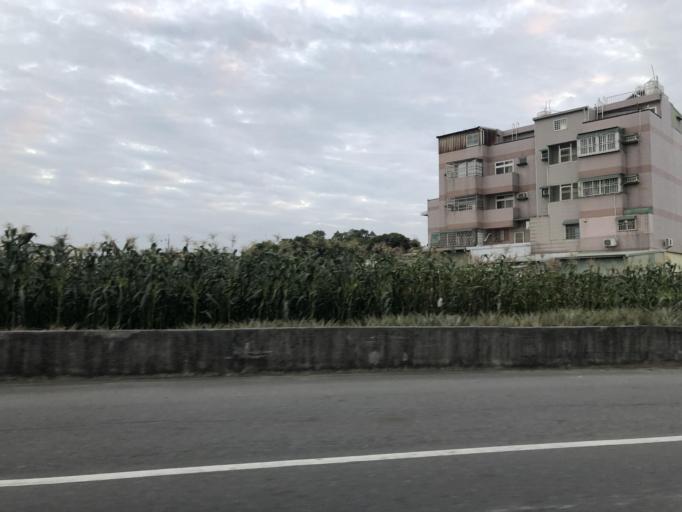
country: TW
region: Taiwan
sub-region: Tainan
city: Tainan
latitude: 23.0227
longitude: 120.3009
